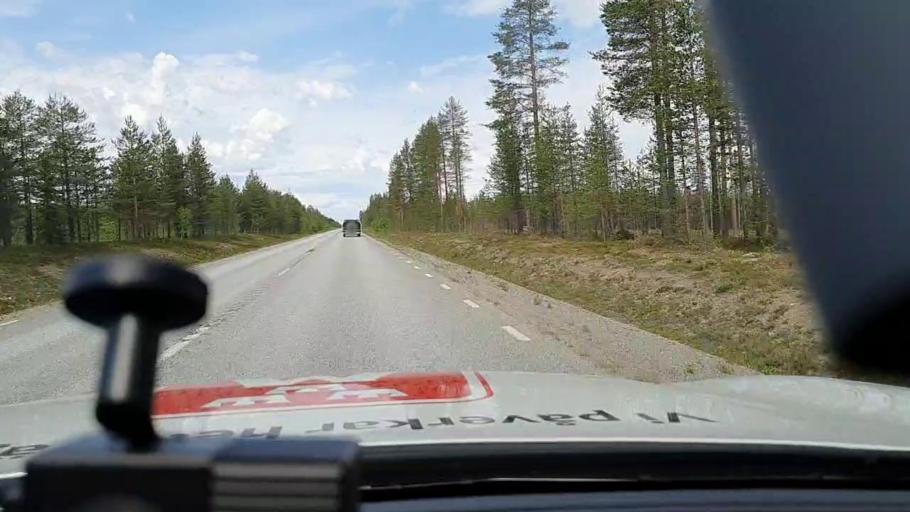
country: SE
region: Norrbotten
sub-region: Jokkmokks Kommun
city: Jokkmokk
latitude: 66.5209
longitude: 20.2134
